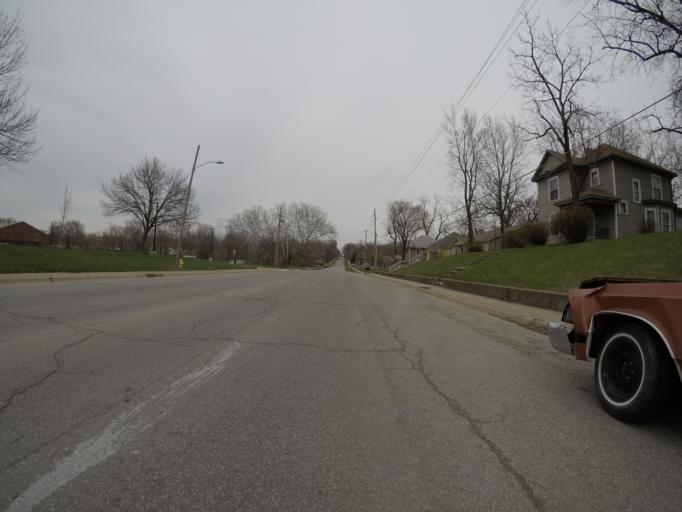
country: US
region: Kansas
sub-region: Johnson County
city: Olathe
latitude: 38.8805
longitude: -94.8168
